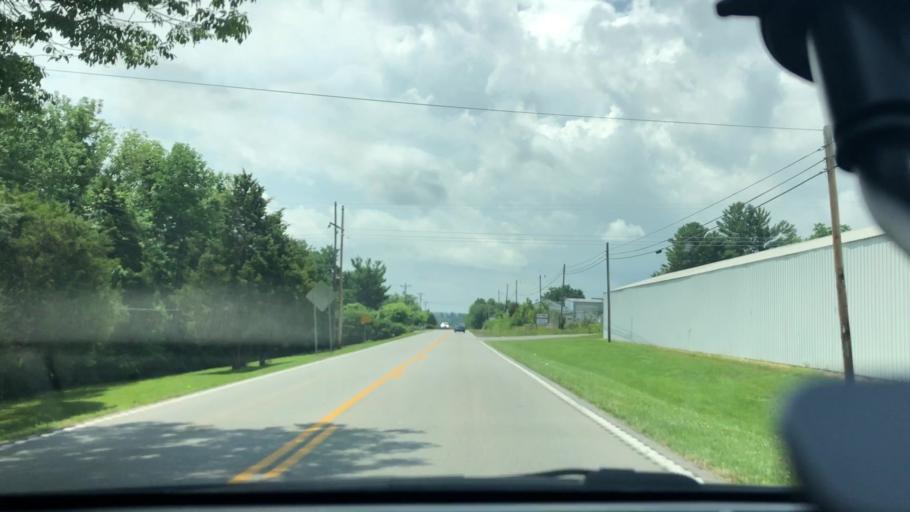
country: US
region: Kentucky
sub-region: Pulaski County
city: Somerset
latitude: 37.0614
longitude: -84.6754
